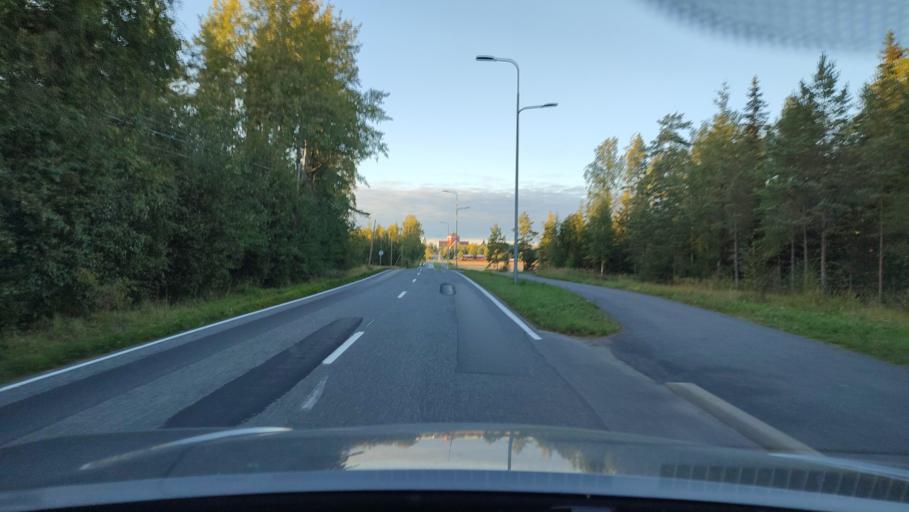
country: FI
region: Ostrobothnia
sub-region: Sydosterbotten
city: Kristinestad
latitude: 62.2373
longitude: 21.5209
